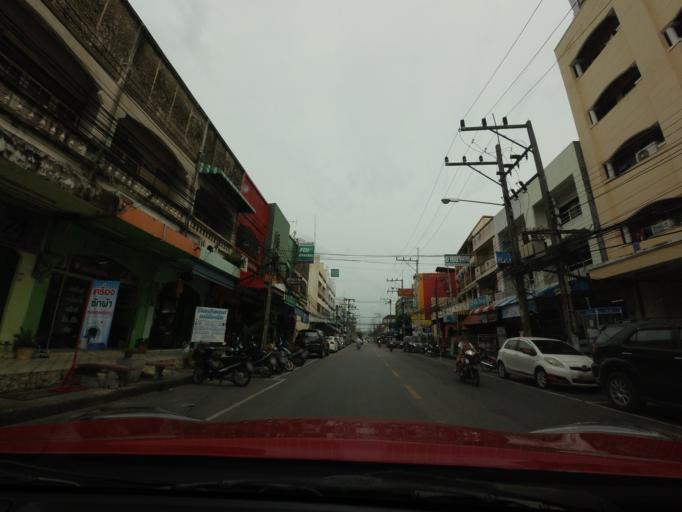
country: TH
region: Songkhla
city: Hat Yai
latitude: 6.9956
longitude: 100.4749
